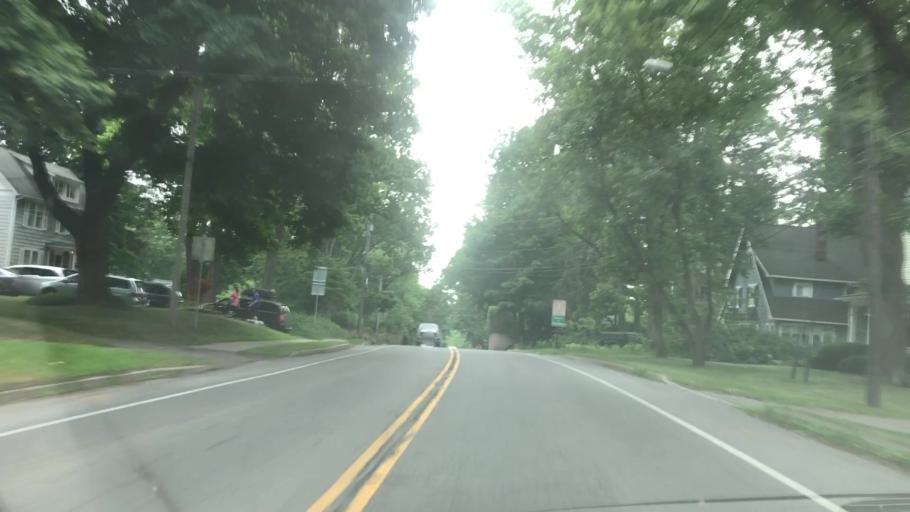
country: US
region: New York
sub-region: Monroe County
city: East Rochester
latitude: 43.1240
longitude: -77.4761
